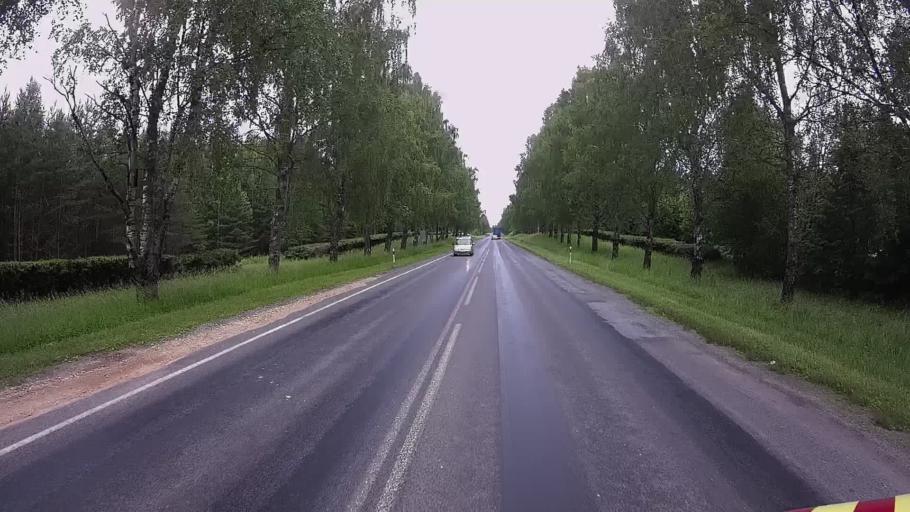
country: EE
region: Viljandimaa
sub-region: Viljandi linn
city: Viljandi
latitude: 58.3007
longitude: 25.5746
